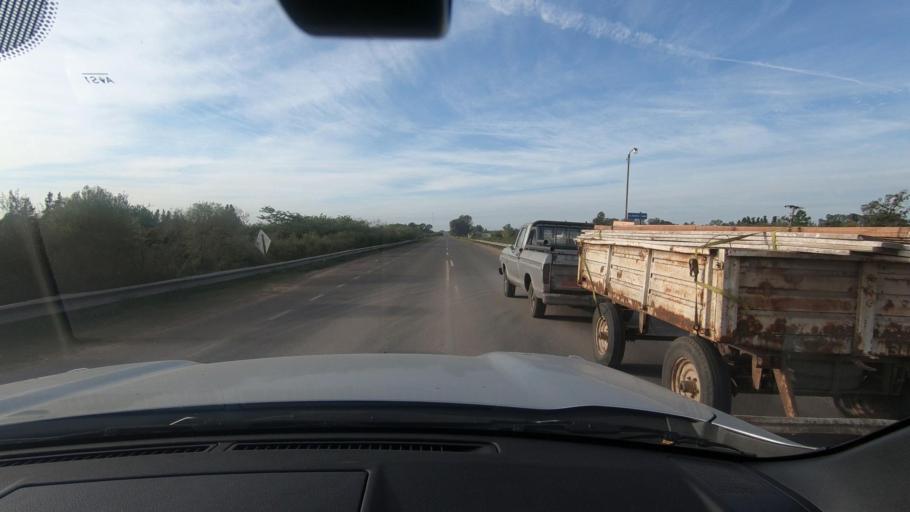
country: AR
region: Entre Rios
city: Colon
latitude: -32.2554
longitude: -58.2195
